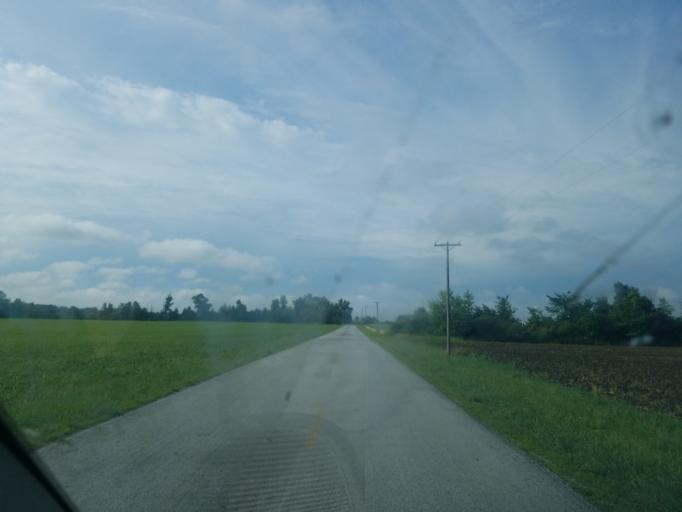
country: US
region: Ohio
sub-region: Hardin County
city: Forest
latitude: 40.7556
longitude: -83.5763
